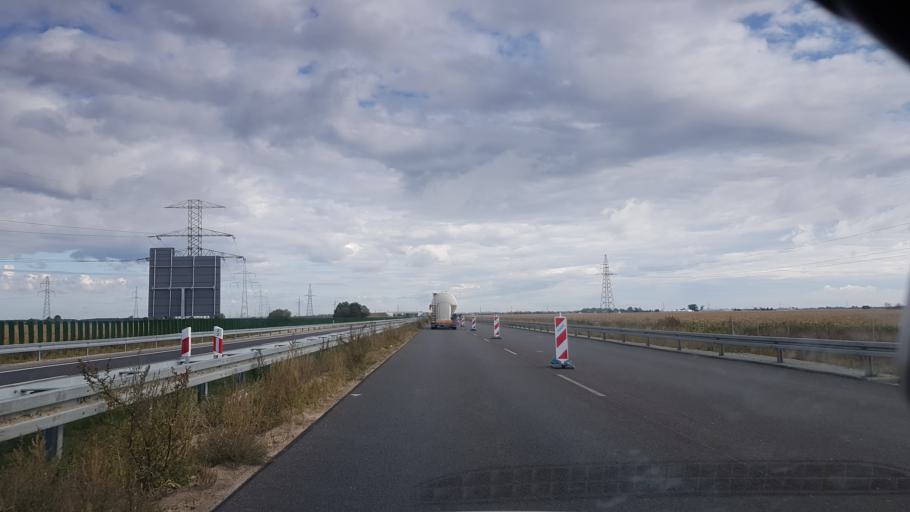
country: PL
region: Greater Poland Voivodeship
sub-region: Powiat poznanski
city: Steszew
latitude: 52.3367
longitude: 16.7395
